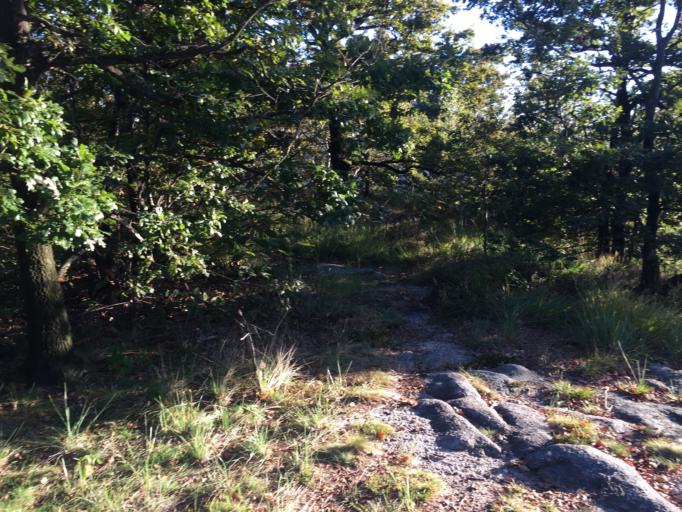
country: IT
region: Piedmont
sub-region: Provincia Verbano-Cusio-Ossola
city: Mergozzo
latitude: 45.9457
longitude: 8.4529
